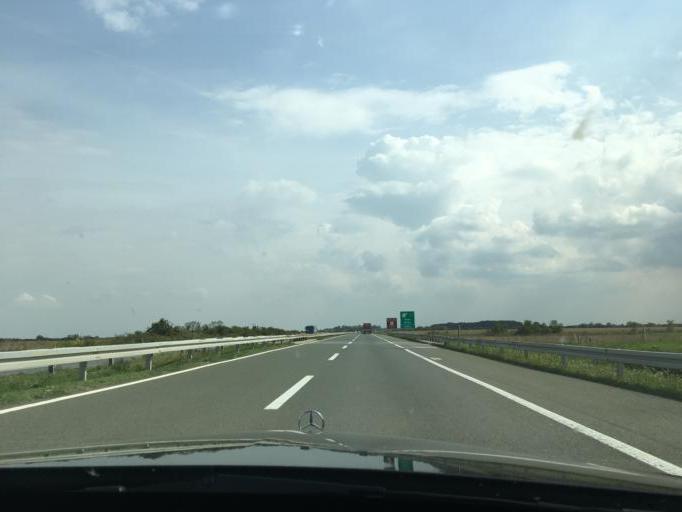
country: RS
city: Sasinci
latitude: 44.9676
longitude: 19.7850
